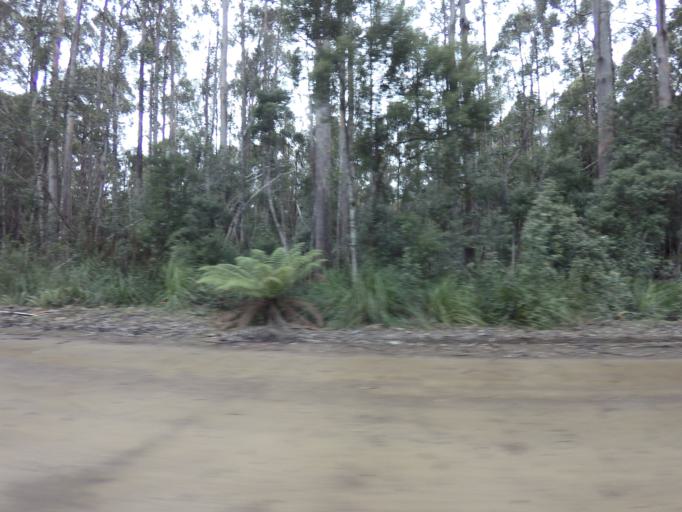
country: AU
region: Tasmania
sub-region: Huon Valley
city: Geeveston
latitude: -43.4916
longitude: 146.8876
